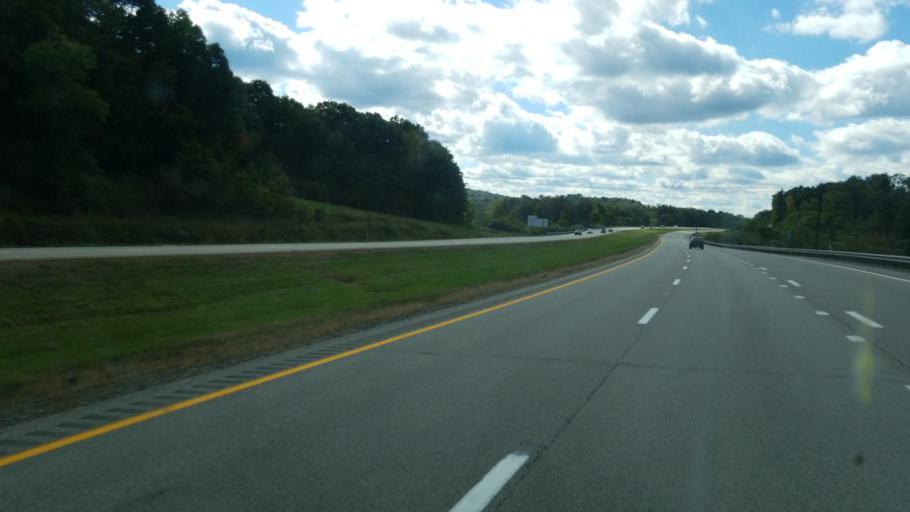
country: US
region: West Virginia
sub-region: Preston County
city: Terra Alta
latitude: 39.6579
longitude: -79.5373
